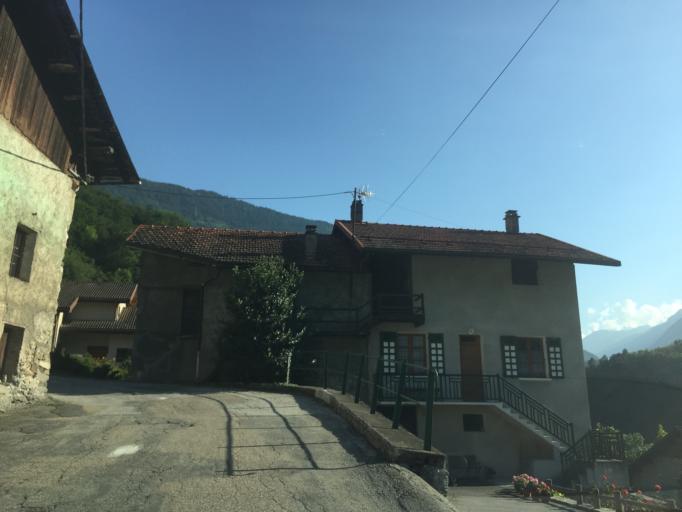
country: FR
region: Rhone-Alpes
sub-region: Departement de la Savoie
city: Moutiers
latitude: 45.5054
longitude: 6.5707
